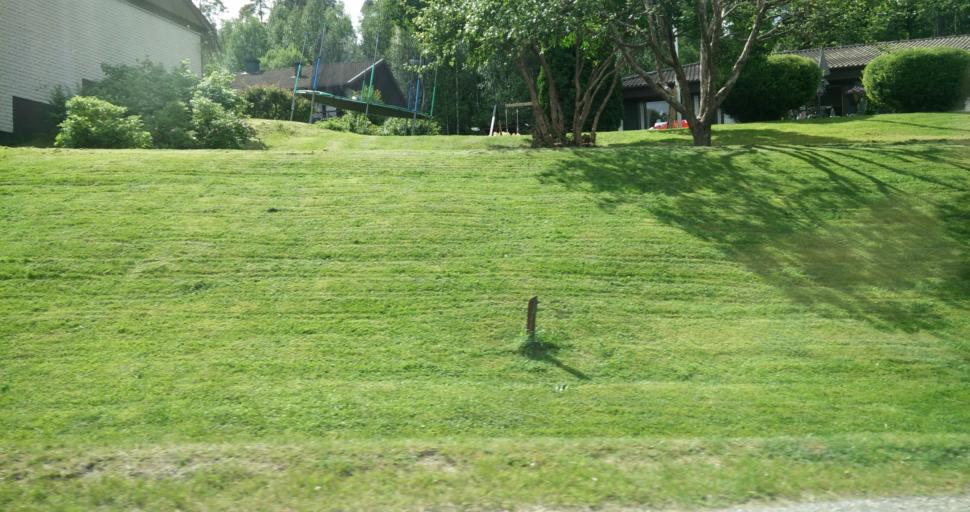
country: SE
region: Vaermland
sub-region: Hagfors Kommun
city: Hagfors
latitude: 60.0218
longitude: 13.6817
